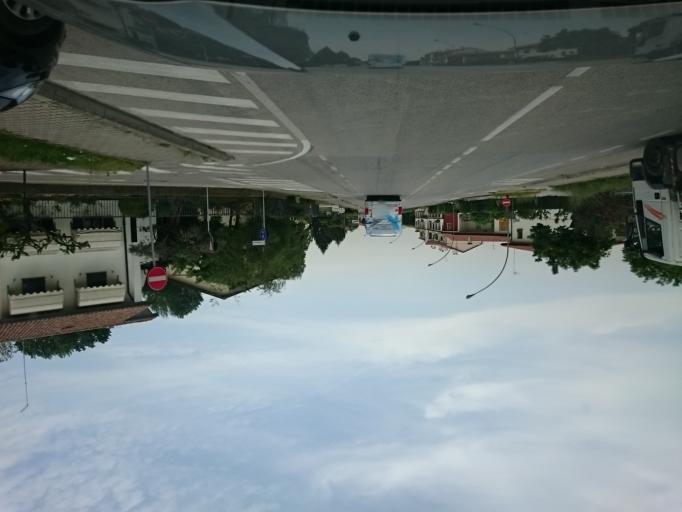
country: IT
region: Veneto
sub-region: Provincia di Venezia
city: Mira Taglio
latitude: 45.4380
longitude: 12.1331
